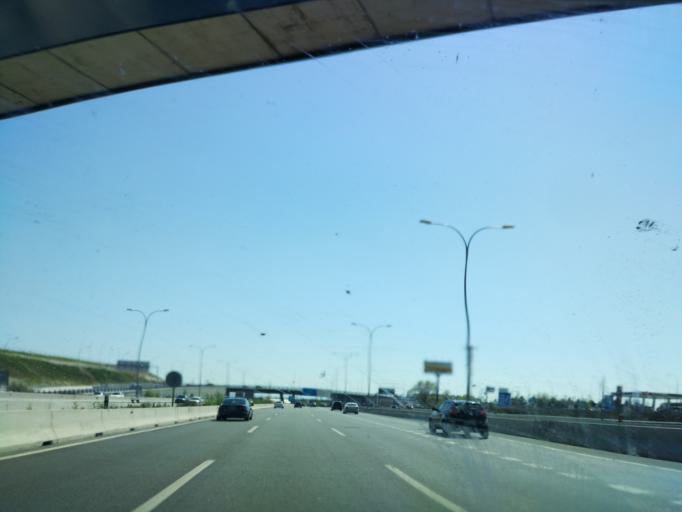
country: ES
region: Madrid
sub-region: Provincia de Madrid
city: Villa de Vallecas
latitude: 40.3699
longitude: -3.5897
